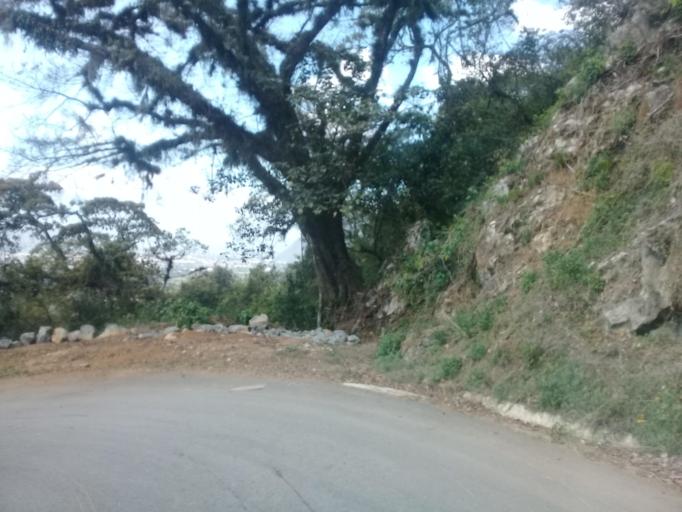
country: MX
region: Veracruz
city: Jalapilla
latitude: 18.8149
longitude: -97.0594
